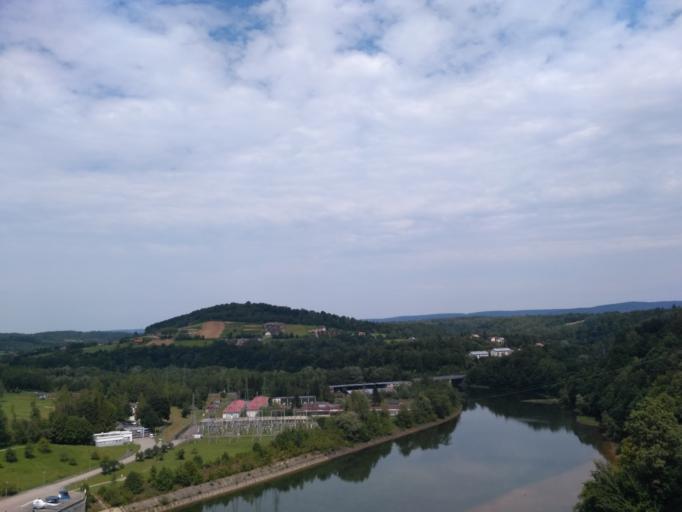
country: PL
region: Subcarpathian Voivodeship
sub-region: Powiat leski
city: Polanczyk
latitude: 49.3945
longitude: 22.4551
